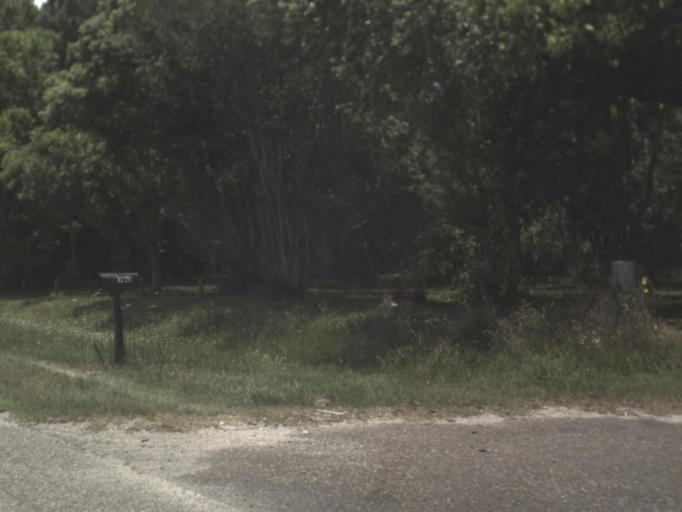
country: US
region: Florida
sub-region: Bradford County
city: Starke
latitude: 29.9086
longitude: -82.1353
